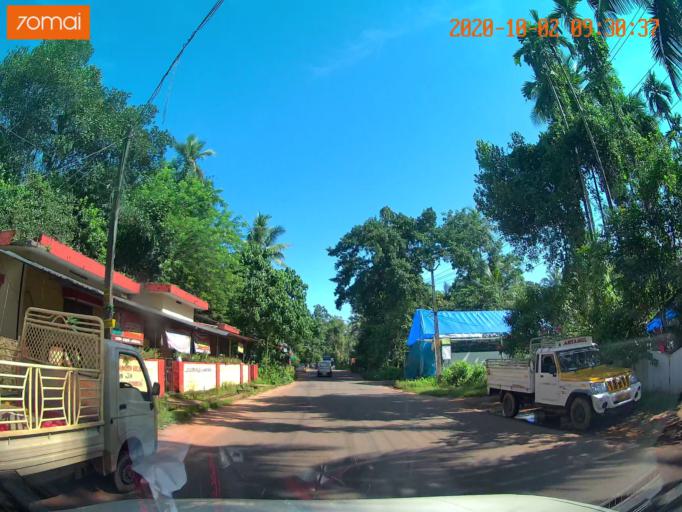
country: IN
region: Kerala
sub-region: Kozhikode
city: Nadapuram
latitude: 11.6186
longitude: 75.7610
